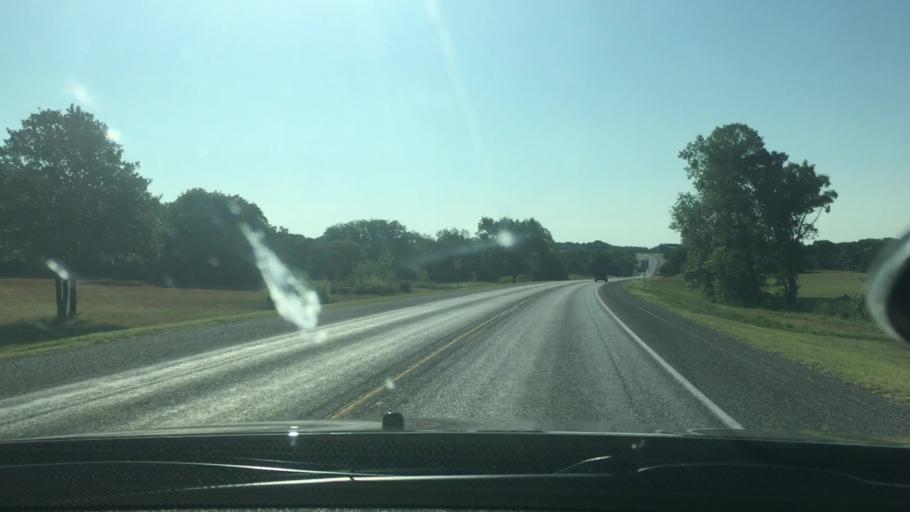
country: US
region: Oklahoma
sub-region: Johnston County
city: Tishomingo
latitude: 34.2410
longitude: -96.7450
